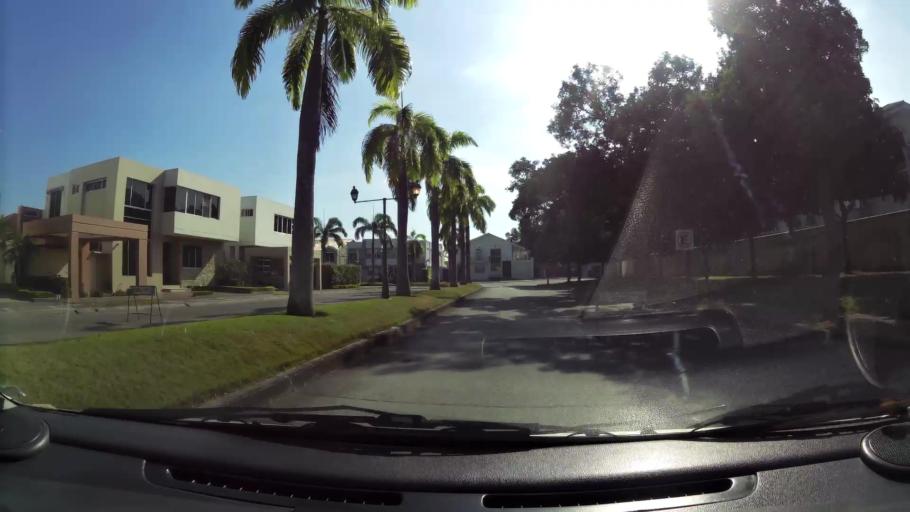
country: EC
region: Guayas
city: Santa Lucia
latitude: -2.1839
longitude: -79.9865
